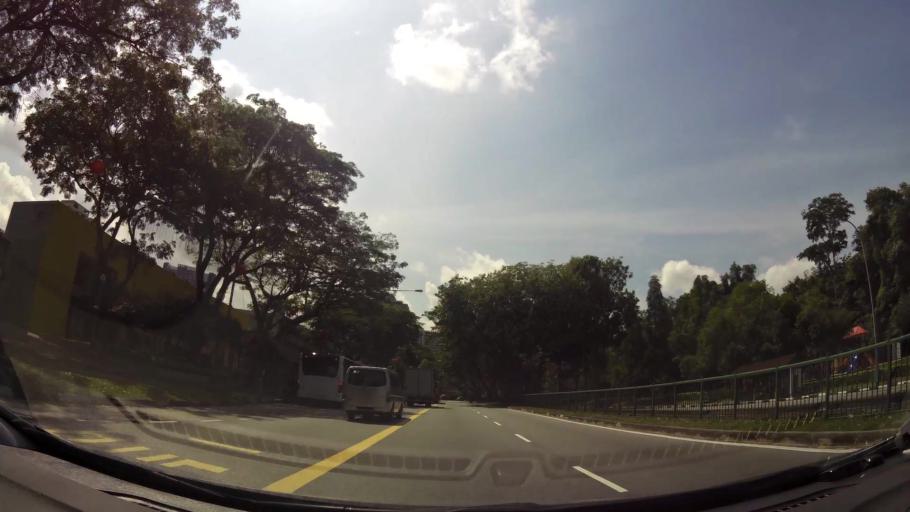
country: SG
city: Singapore
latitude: 1.3737
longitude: 103.8452
